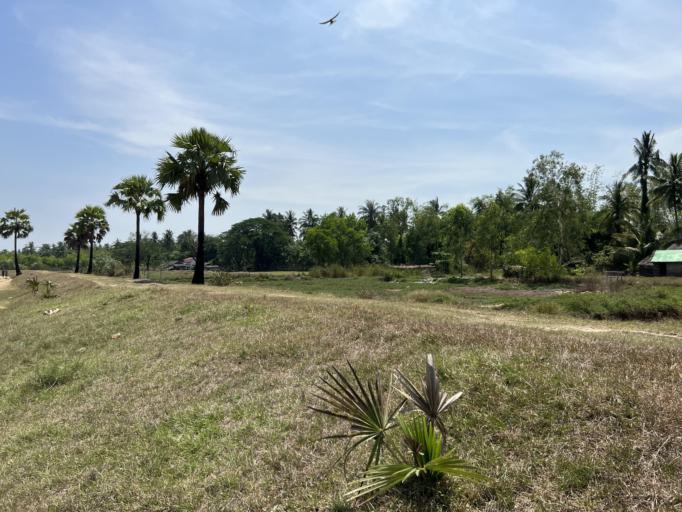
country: MM
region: Ayeyarwady
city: Pyapon
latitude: 15.9015
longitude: 95.6126
